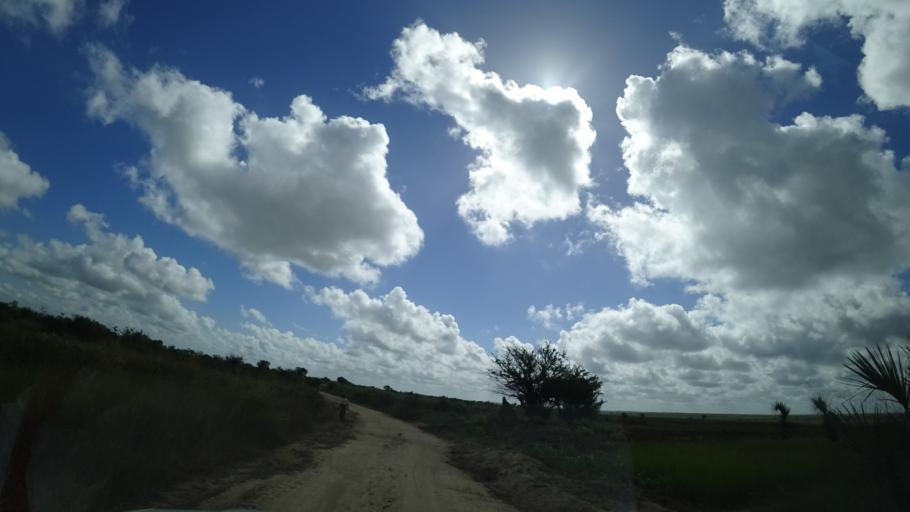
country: MZ
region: Sofala
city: Dondo
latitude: -19.4174
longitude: 34.5655
